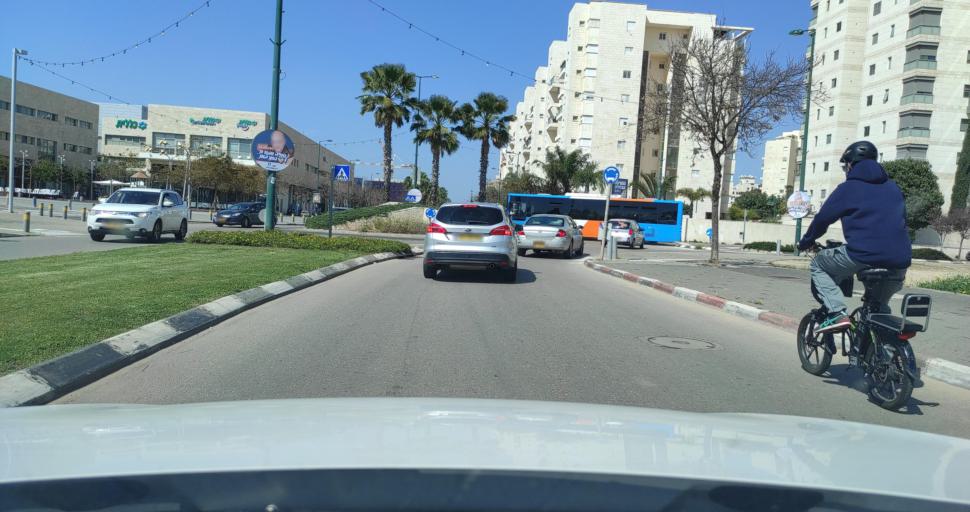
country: IL
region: Central District
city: Nordiyya
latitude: 32.3058
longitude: 34.8697
